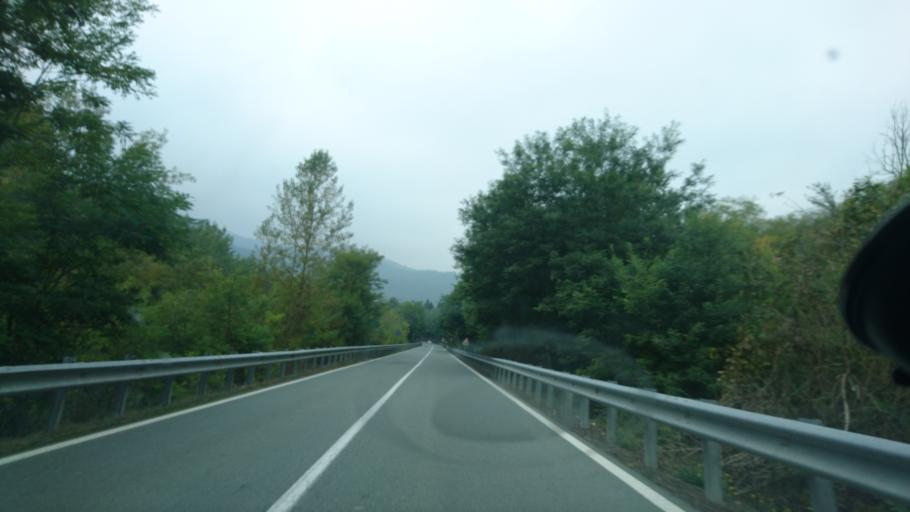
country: IT
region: Piedmont
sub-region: Provincia di Alessandria
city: Ponti
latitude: 44.6107
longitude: 8.3540
